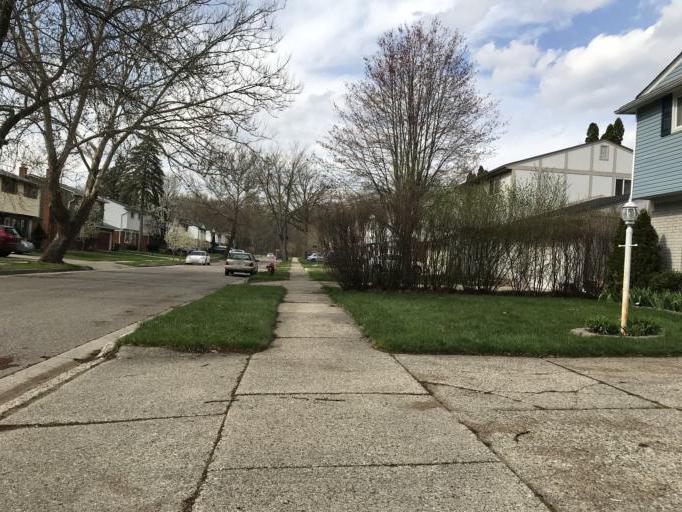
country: US
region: Michigan
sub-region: Oakland County
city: Farmington
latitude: 42.4613
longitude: -83.3416
